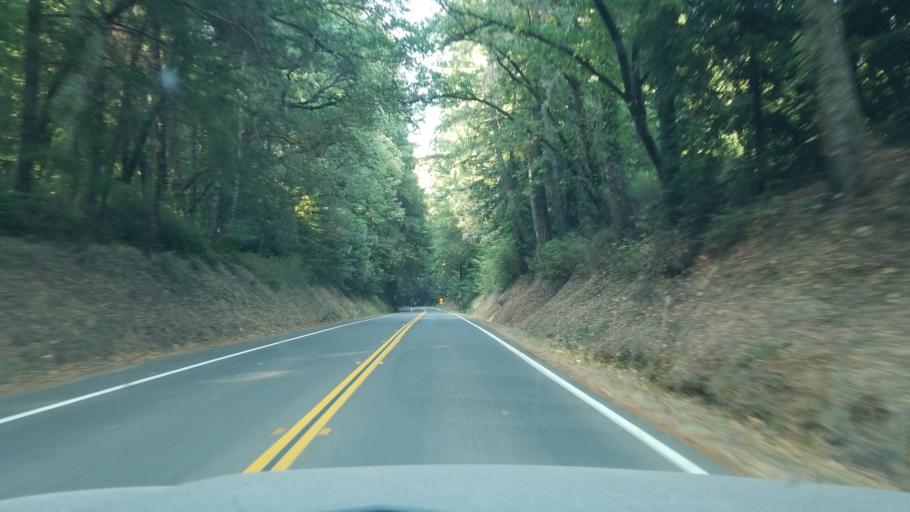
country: US
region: California
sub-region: Humboldt County
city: Redway
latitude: 40.2391
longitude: -123.8230
